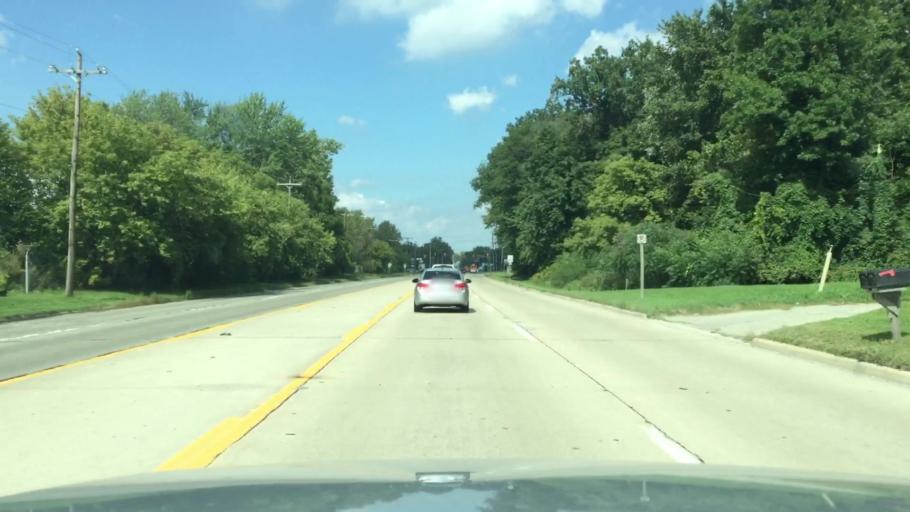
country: US
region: Michigan
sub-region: Wayne County
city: Wayne
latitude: 42.2641
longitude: -83.3480
